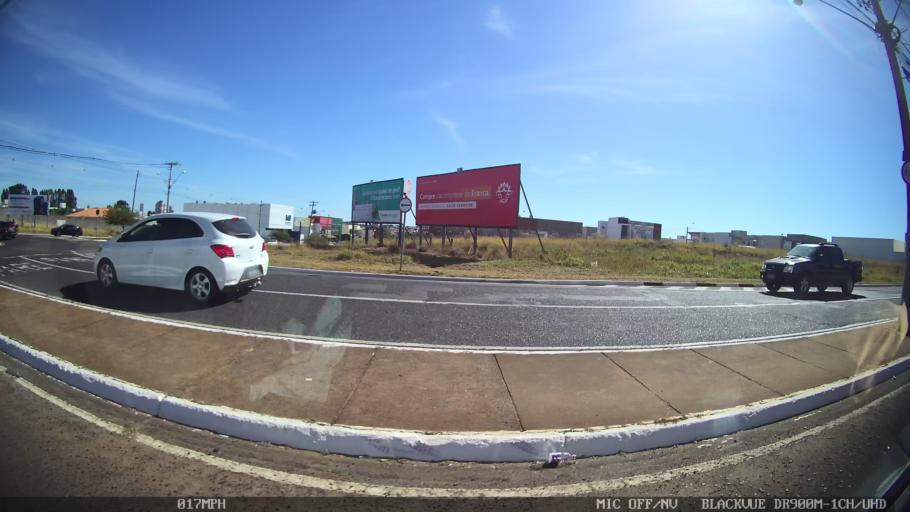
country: BR
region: Sao Paulo
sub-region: Franca
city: Franca
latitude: -20.5419
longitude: -47.3742
